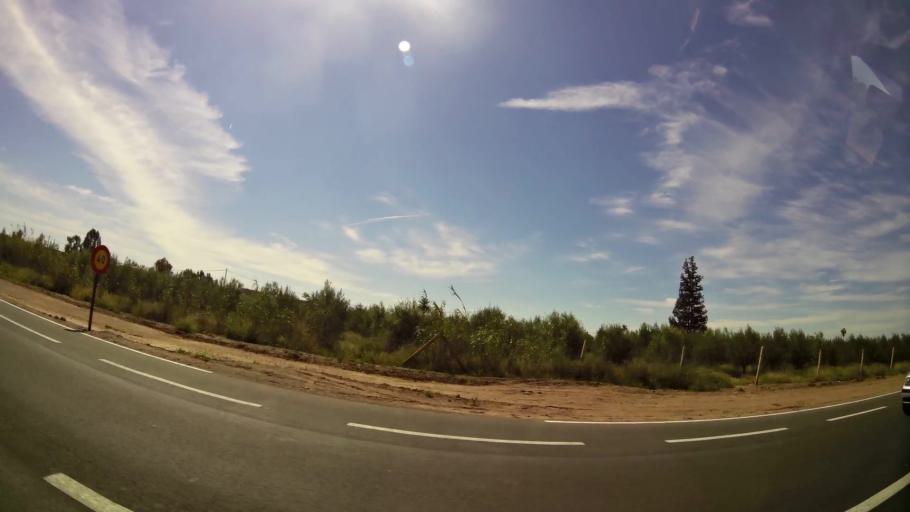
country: MA
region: Marrakech-Tensift-Al Haouz
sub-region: Marrakech
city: Marrakesh
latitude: 31.6437
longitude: -8.1053
